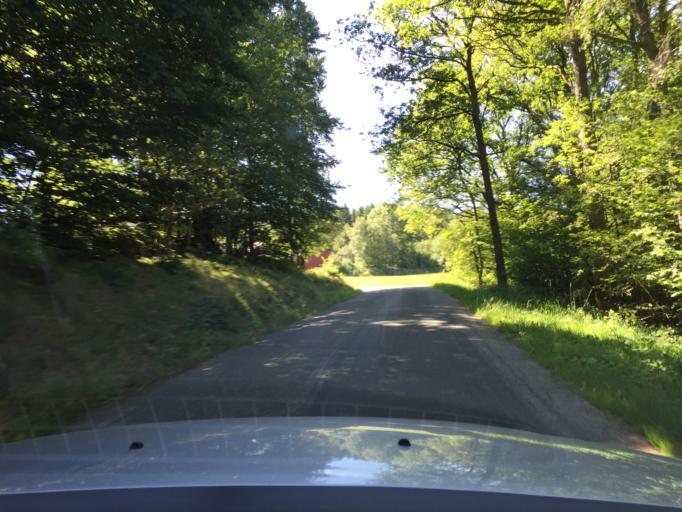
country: SE
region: Skane
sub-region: Hassleholms Kommun
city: Sosdala
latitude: 56.0214
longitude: 13.5822
